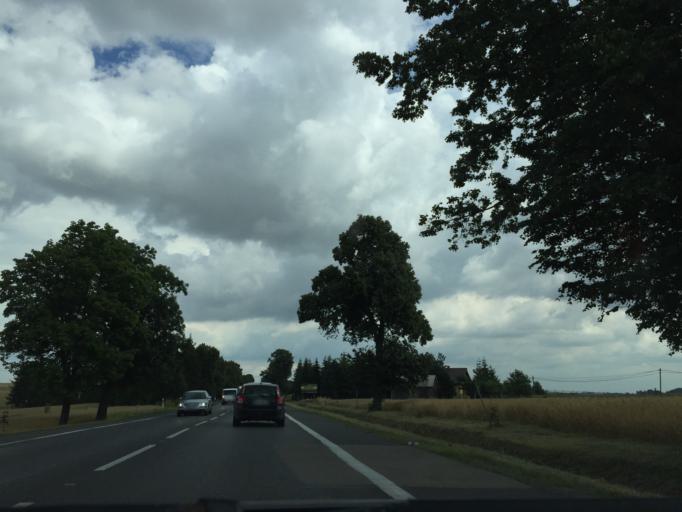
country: PL
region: Lesser Poland Voivodeship
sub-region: Powiat krakowski
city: Slomniki
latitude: 50.2263
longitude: 20.0498
